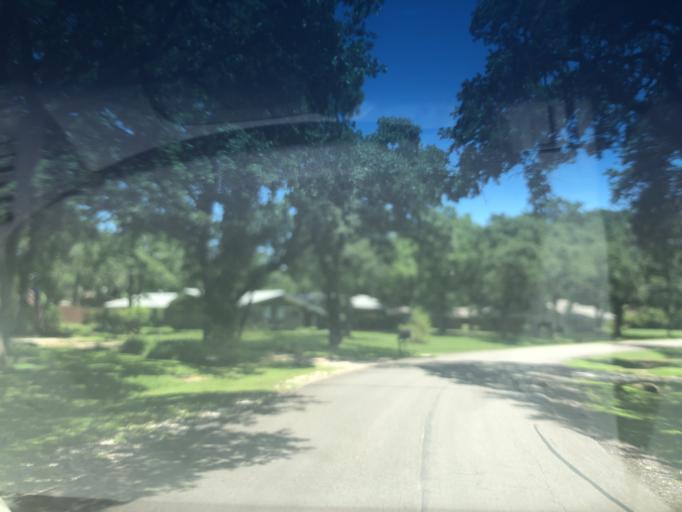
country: US
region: Texas
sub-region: Dallas County
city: Grand Prairie
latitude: 32.7781
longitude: -97.0297
